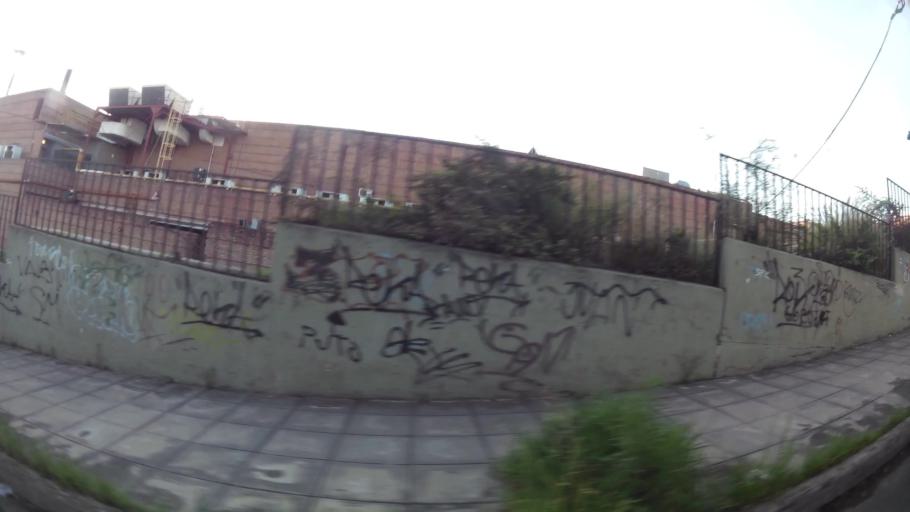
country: AR
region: Cordoba
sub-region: Departamento de Capital
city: Cordoba
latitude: -31.3812
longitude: -64.2135
